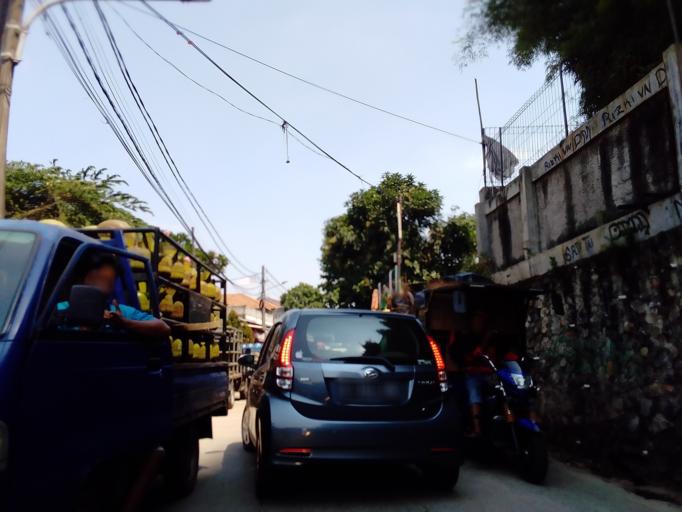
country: ID
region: Jakarta Raya
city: Jakarta
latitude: -6.2598
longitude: 106.8043
